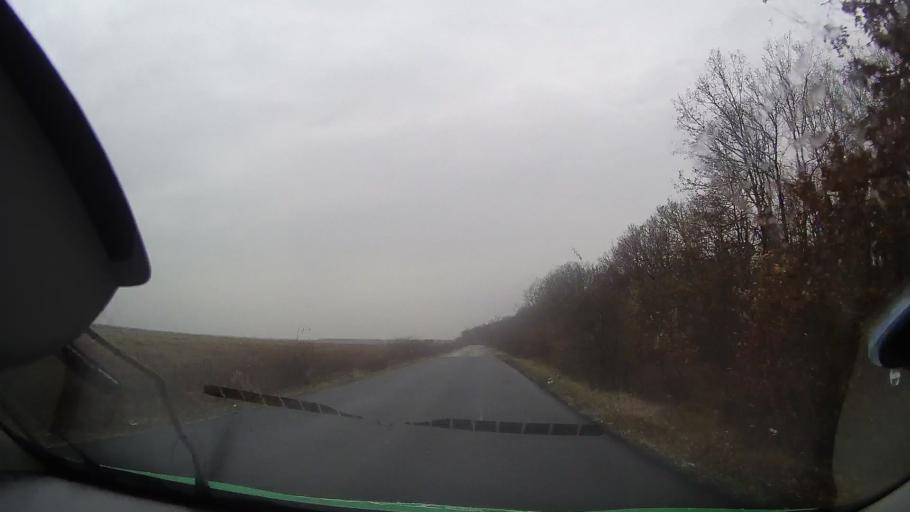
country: RO
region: Bihor
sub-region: Comuna Tinca
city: Gurbediu
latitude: 46.7784
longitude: 21.8762
